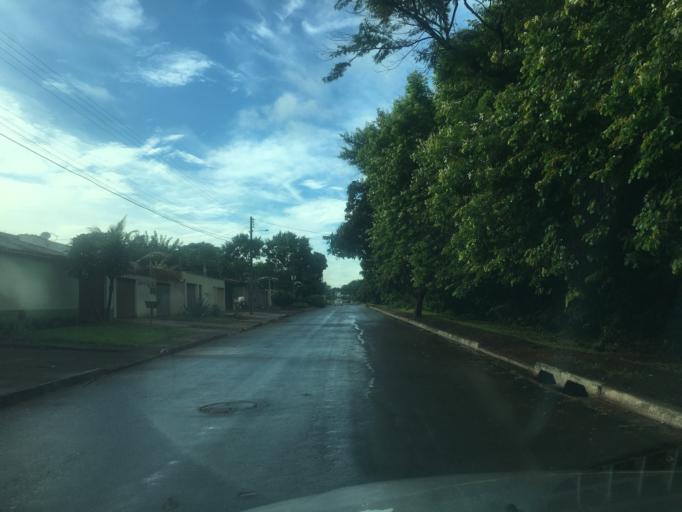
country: BR
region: Goias
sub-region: Aparecida De Goiania
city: Aparecida de Goiania
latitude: -16.7994
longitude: -49.2470
